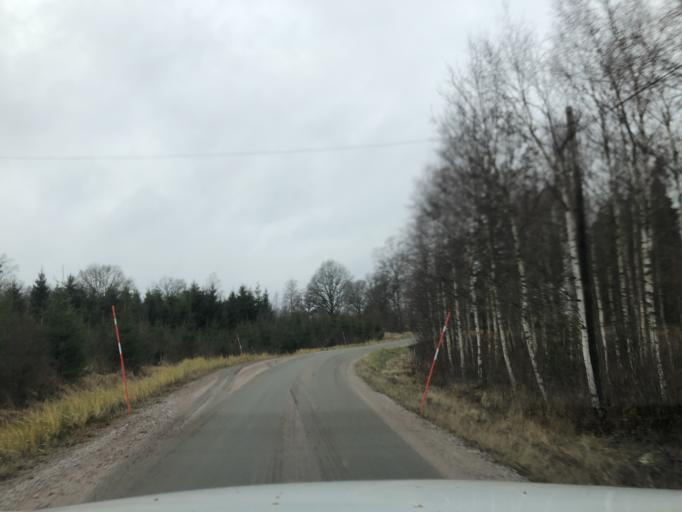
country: SE
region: Vaestra Goetaland
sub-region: Ulricehamns Kommun
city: Ulricehamn
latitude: 57.8614
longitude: 13.5956
